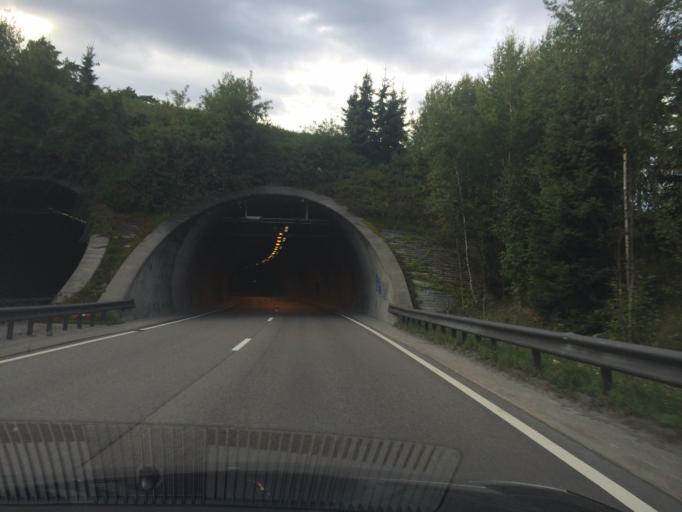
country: NO
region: Oslo
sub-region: Oslo
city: Oslo
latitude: 59.8979
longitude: 10.8043
